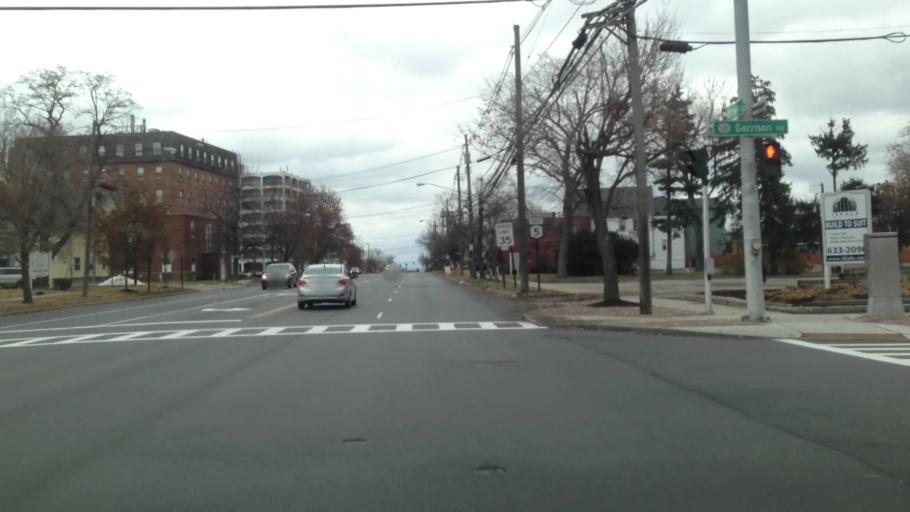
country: US
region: New York
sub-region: Erie County
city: Williamsville
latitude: 42.9639
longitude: -78.7381
